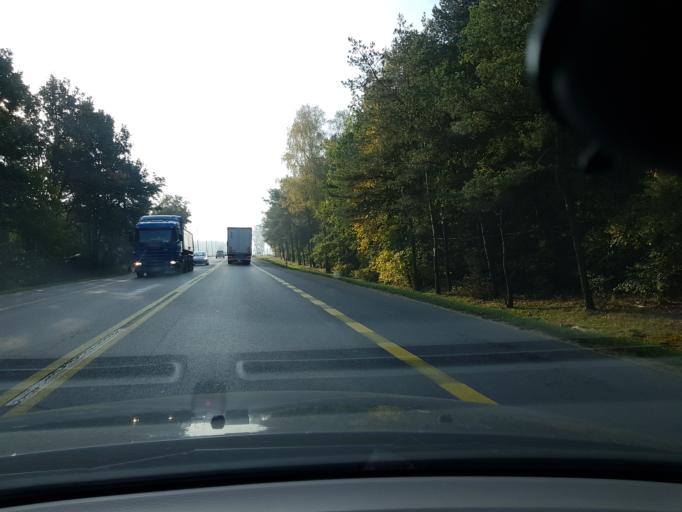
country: PL
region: Masovian Voivodeship
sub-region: Powiat otwocki
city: Otwock
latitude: 52.1475
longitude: 21.3212
